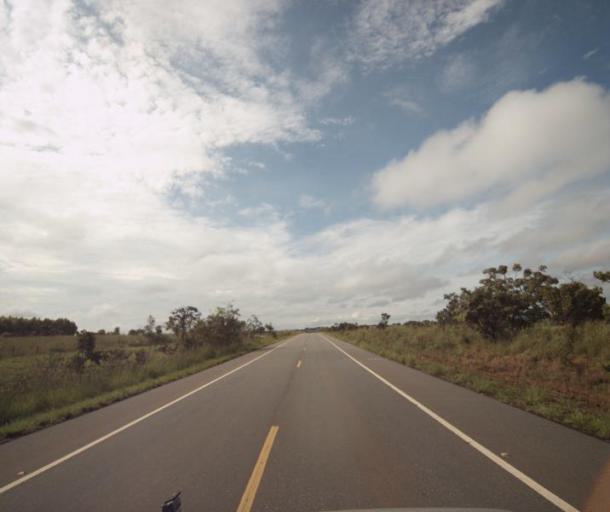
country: BR
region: Goias
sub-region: Padre Bernardo
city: Padre Bernardo
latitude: -15.3264
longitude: -48.6534
